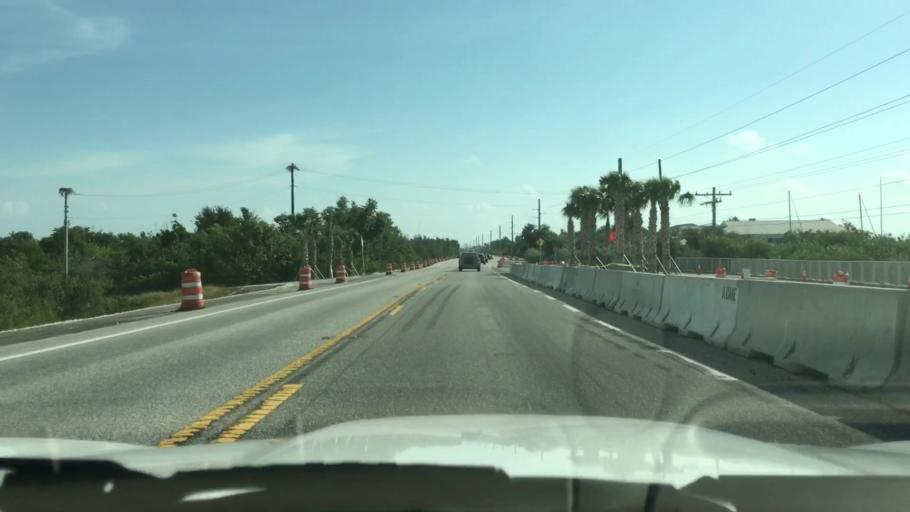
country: US
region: Florida
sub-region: Monroe County
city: Cudjoe Key
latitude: 24.6626
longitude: -81.4629
